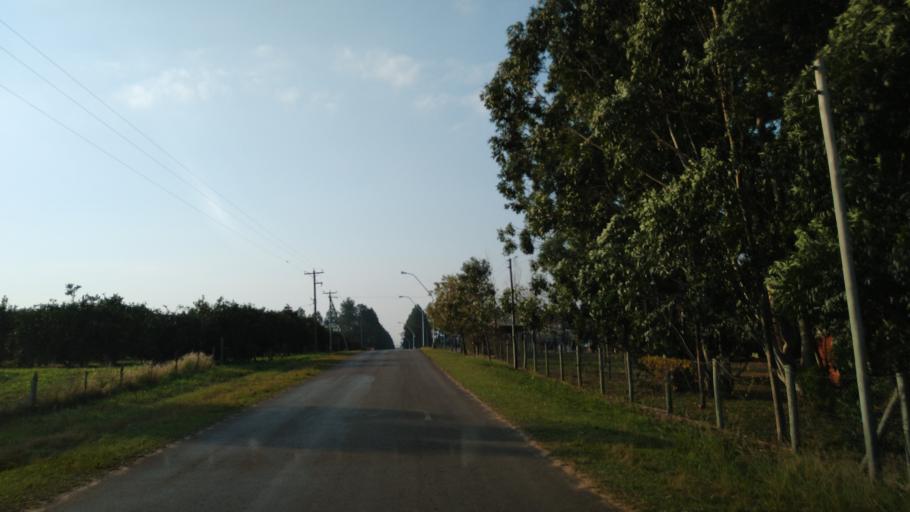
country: AR
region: Entre Rios
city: Santa Ana
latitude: -30.9113
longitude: -57.9265
